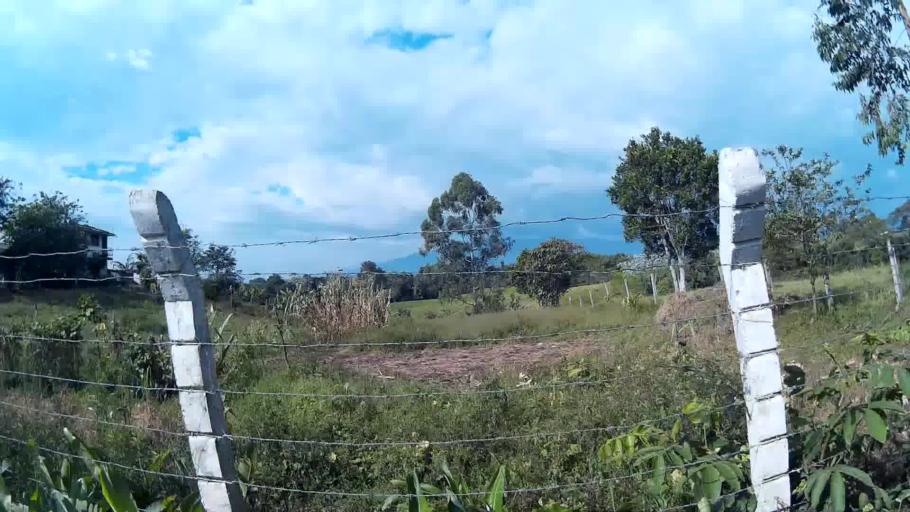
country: CO
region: Quindio
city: Filandia
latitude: 4.6982
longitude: -75.6789
